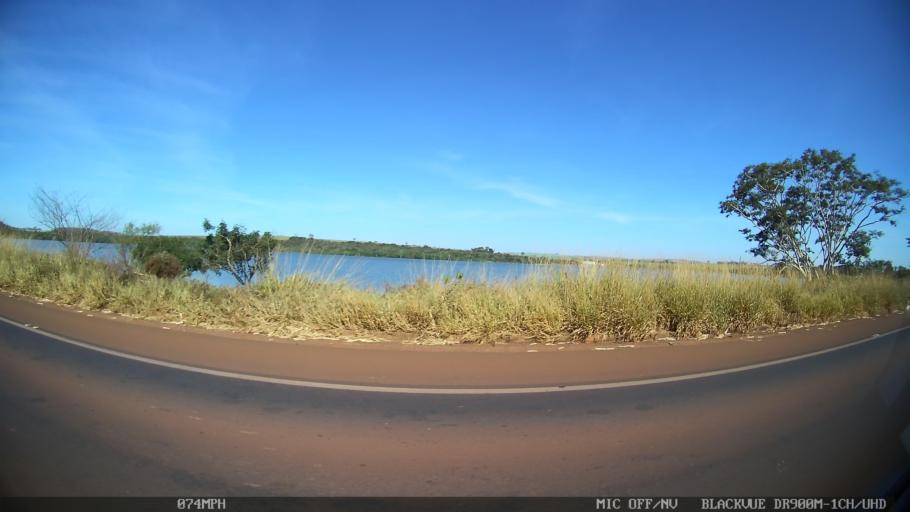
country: BR
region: Sao Paulo
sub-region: Sao Joaquim Da Barra
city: Sao Joaquim da Barra
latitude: -20.5408
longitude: -47.8089
